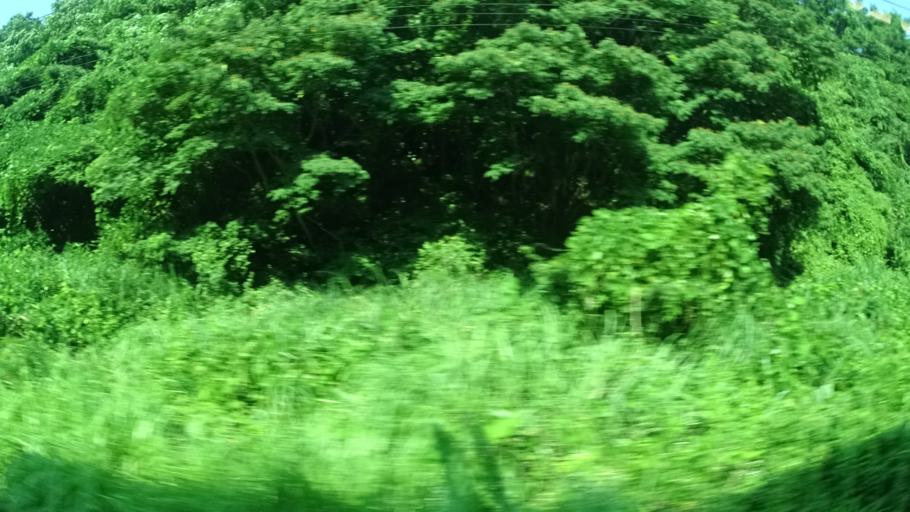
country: JP
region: Fukushima
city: Iwaki
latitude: 37.1668
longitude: 140.9983
